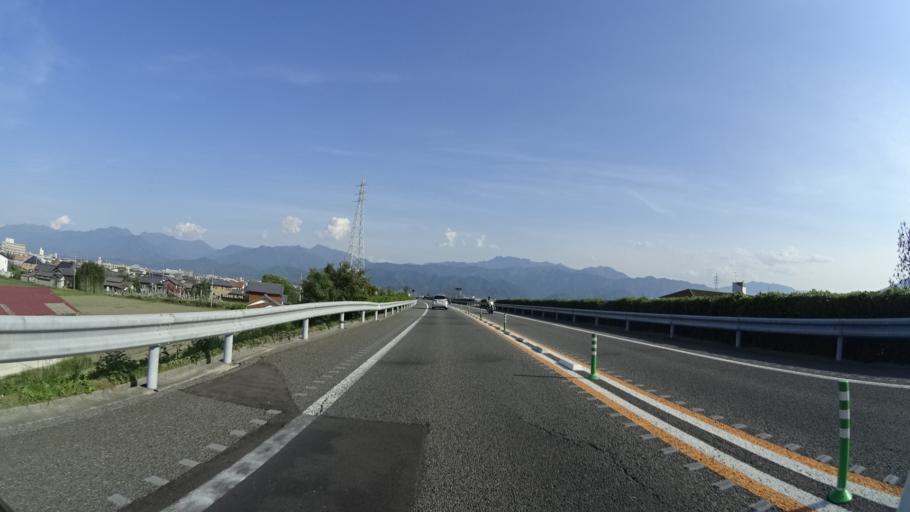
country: JP
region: Ehime
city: Saijo
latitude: 33.9337
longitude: 133.0700
